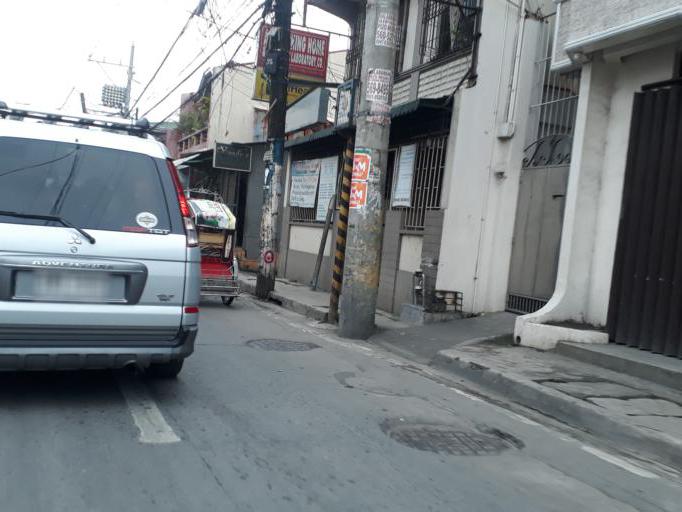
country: PH
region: Calabarzon
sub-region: Province of Rizal
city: Malabon
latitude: 14.6656
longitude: 120.9415
